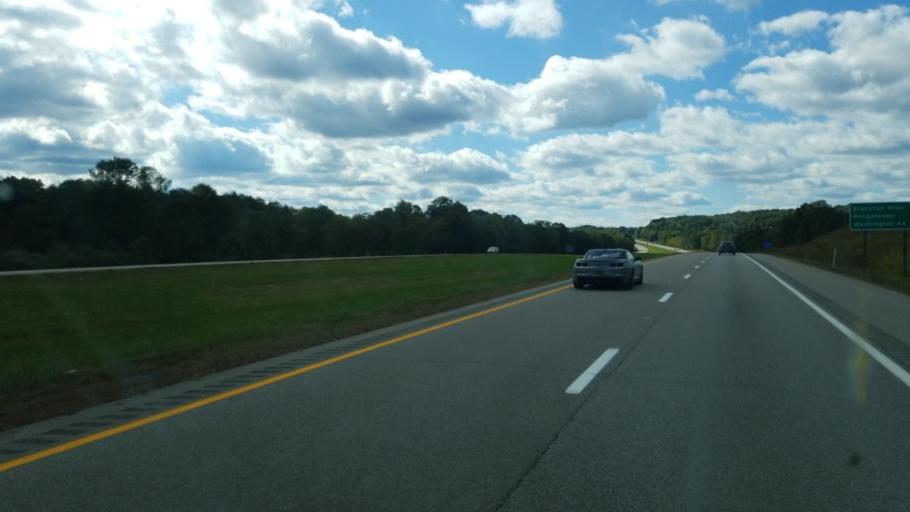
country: US
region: West Virginia
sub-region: Preston County
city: Terra Alta
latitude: 39.6568
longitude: -79.5480
